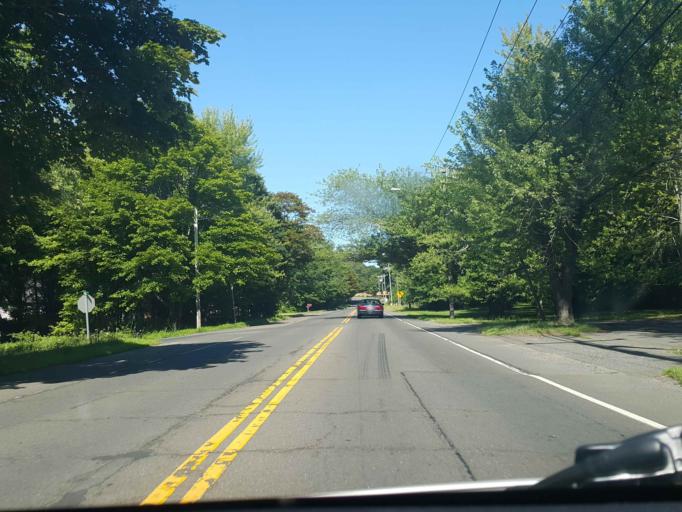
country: US
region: Connecticut
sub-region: New Haven County
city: North Branford
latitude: 41.3110
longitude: -72.7373
